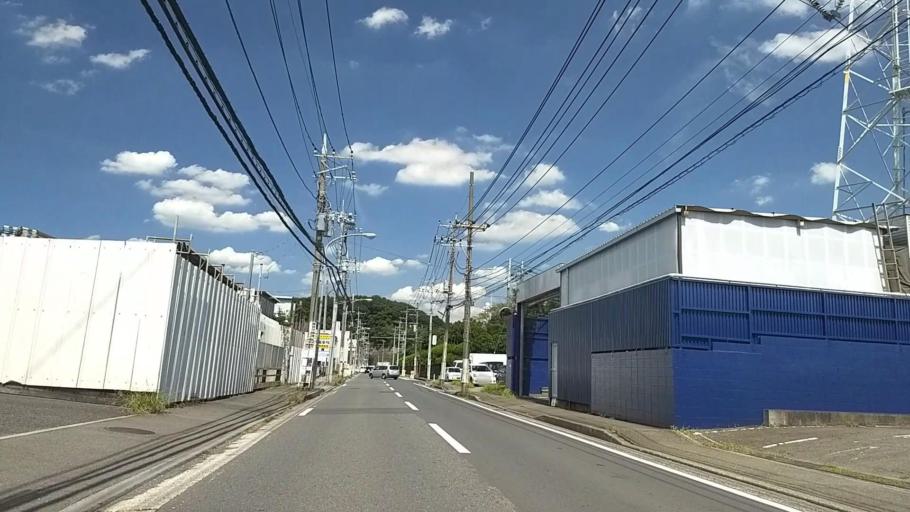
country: JP
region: Kanagawa
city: Yokohama
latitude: 35.5161
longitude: 139.5808
